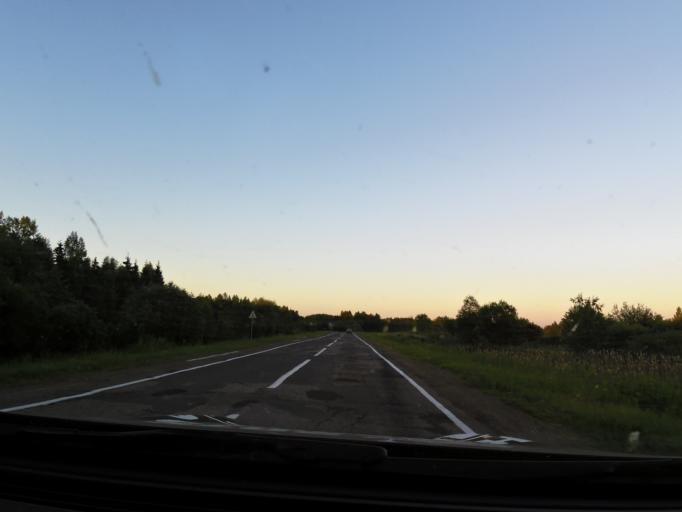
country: RU
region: Jaroslavl
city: Lyubim
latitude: 58.3558
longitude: 40.6240
